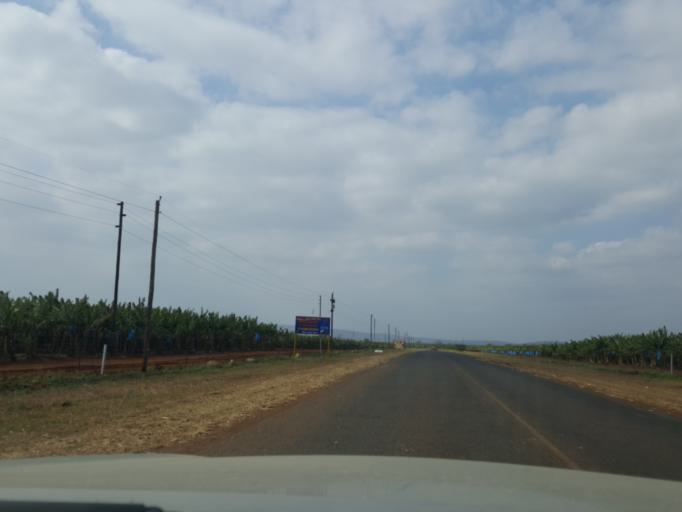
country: ZA
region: Mpumalanga
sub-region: Ehlanzeni District
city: Komatipoort
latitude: -25.3915
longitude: 31.9061
